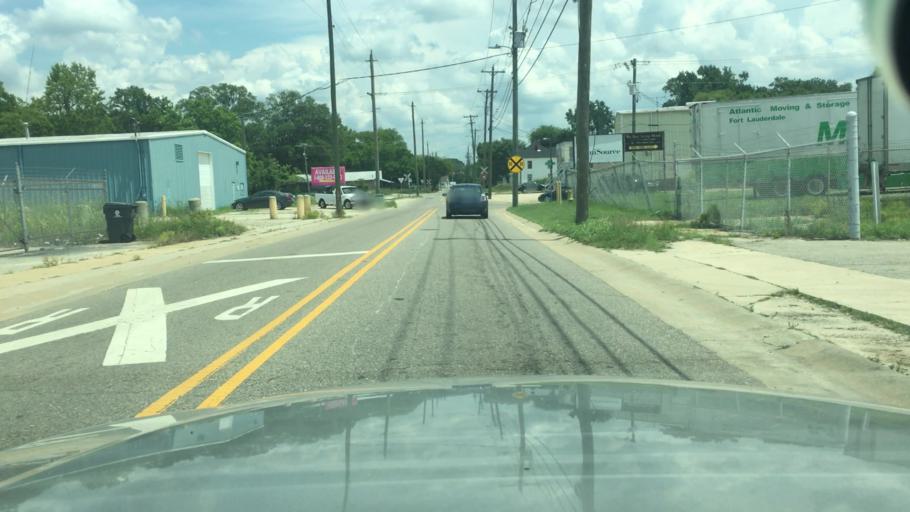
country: US
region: North Carolina
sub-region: Cumberland County
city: Fayetteville
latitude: 35.0472
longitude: -78.8844
